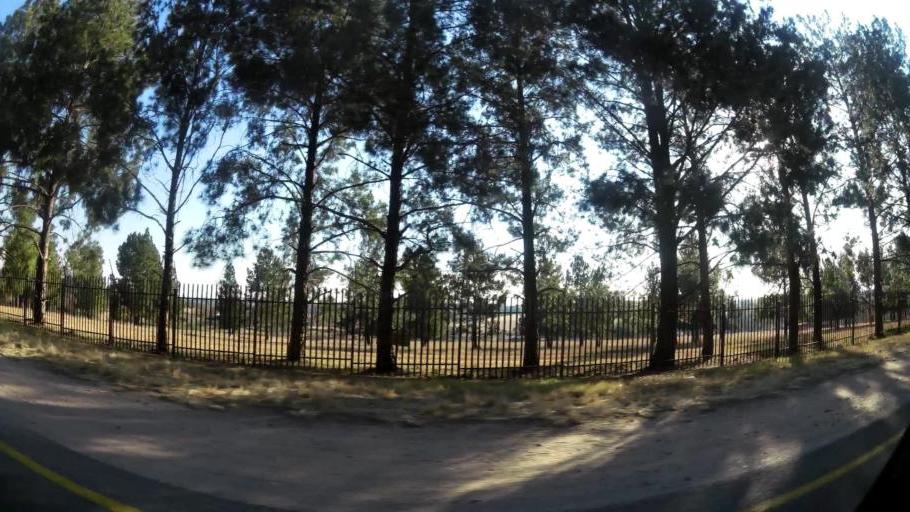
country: ZA
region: Gauteng
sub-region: West Rand District Municipality
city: Muldersdriseloop
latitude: -26.0283
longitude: 27.9085
